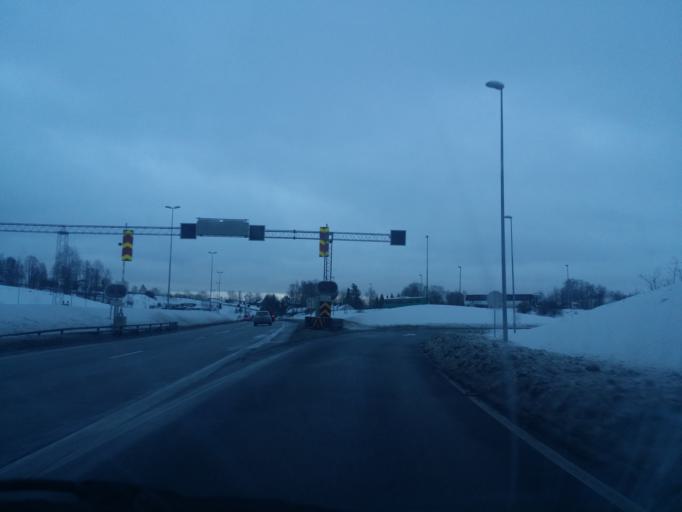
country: NO
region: Akershus
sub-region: Baerum
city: Skui
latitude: 59.9238
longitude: 10.4611
